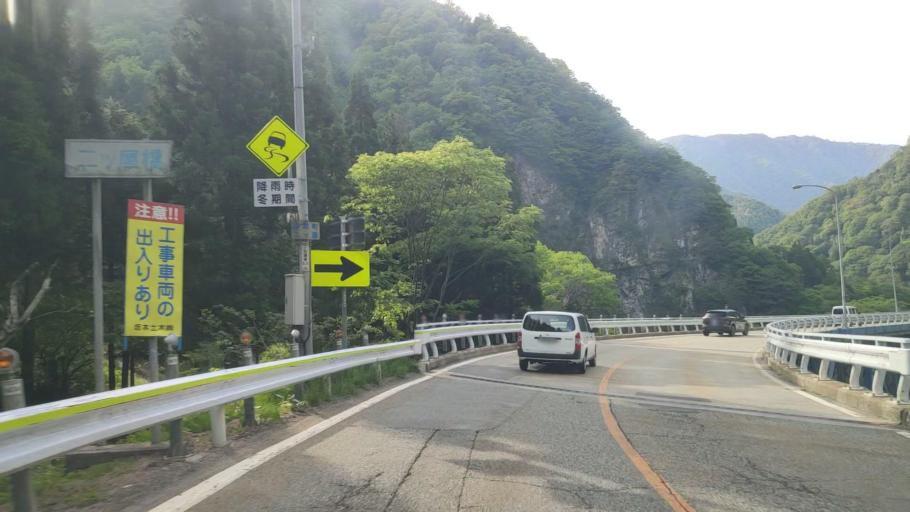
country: JP
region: Gifu
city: Takayama
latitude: 36.3678
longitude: 137.2829
